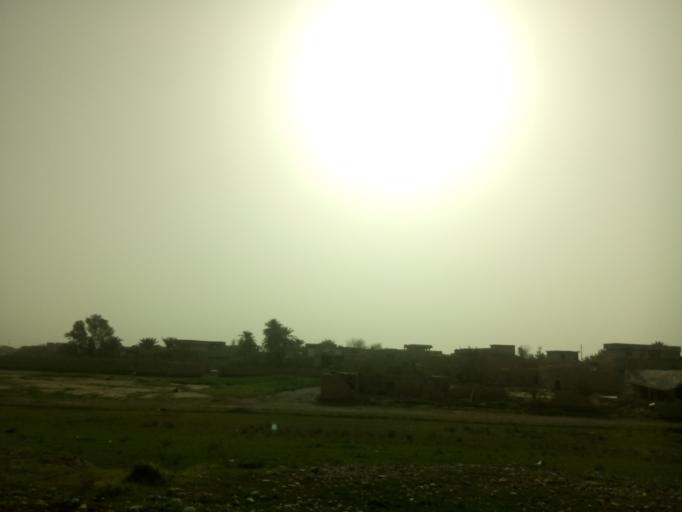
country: IQ
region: Salah ad Din Governorate
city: Tozkhurmato
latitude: 34.7819
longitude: 44.5781
